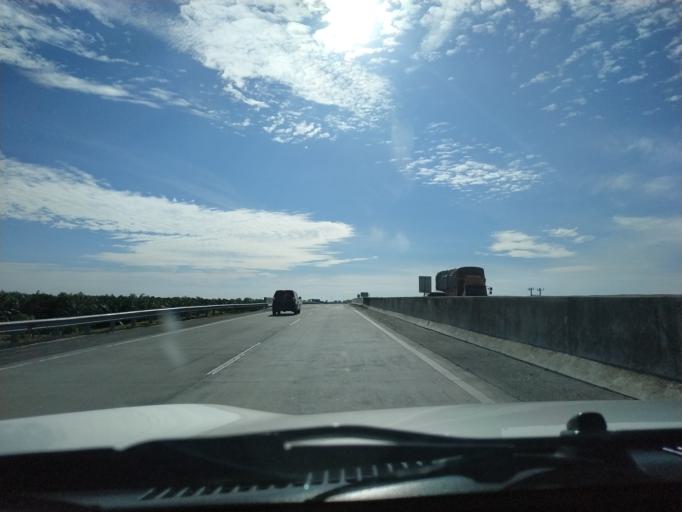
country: ID
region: North Sumatra
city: Percut
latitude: 3.5354
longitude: 98.8617
